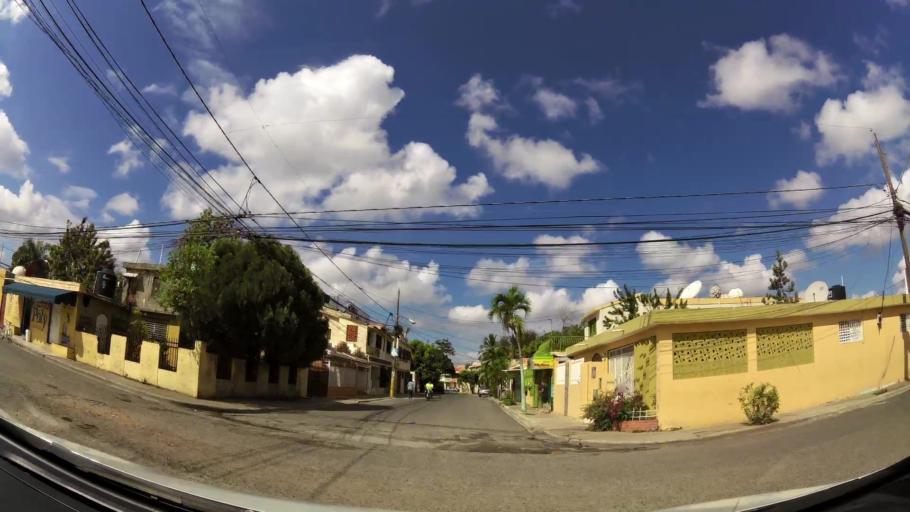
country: DO
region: Santo Domingo
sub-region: Santo Domingo
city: Santo Domingo Este
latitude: 18.5095
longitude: -69.8471
